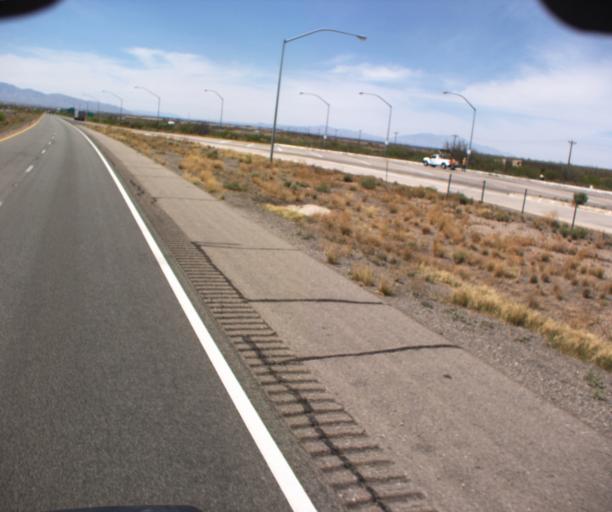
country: US
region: New Mexico
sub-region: Hidalgo County
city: Lordsburg
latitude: 32.2575
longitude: -109.1806
